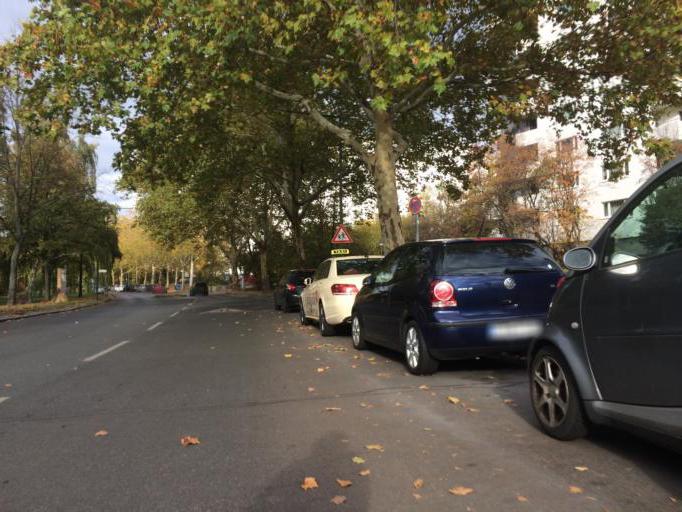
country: DE
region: Berlin
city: Markisches Viertel
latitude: 52.6041
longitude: 13.3494
